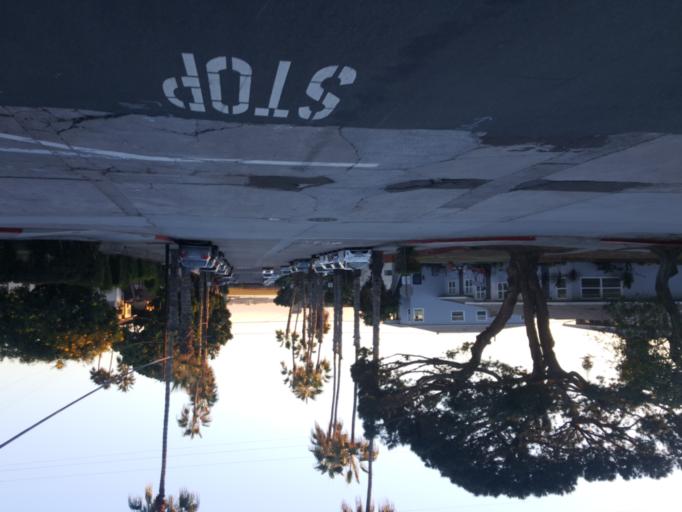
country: US
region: California
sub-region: San Diego County
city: La Jolla
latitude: 32.7982
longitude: -117.2306
